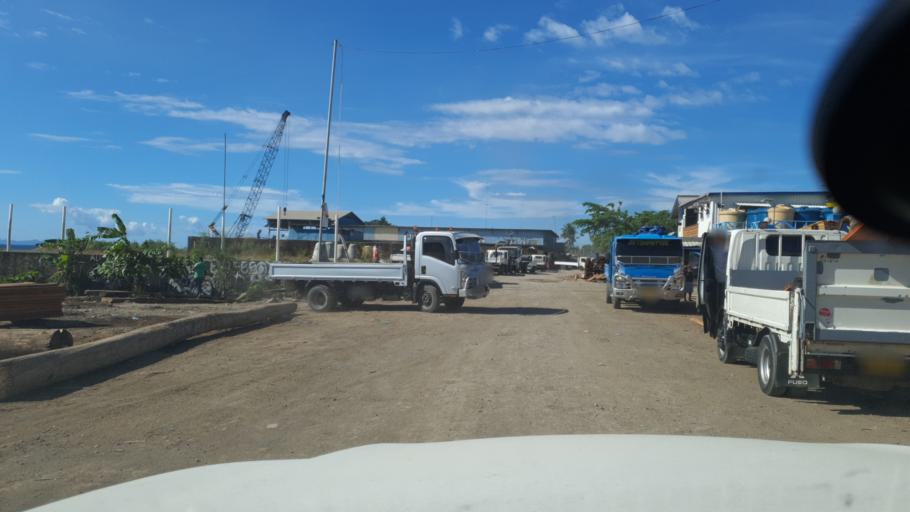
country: SB
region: Guadalcanal
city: Honiara
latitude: -9.4224
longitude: 160.0085
